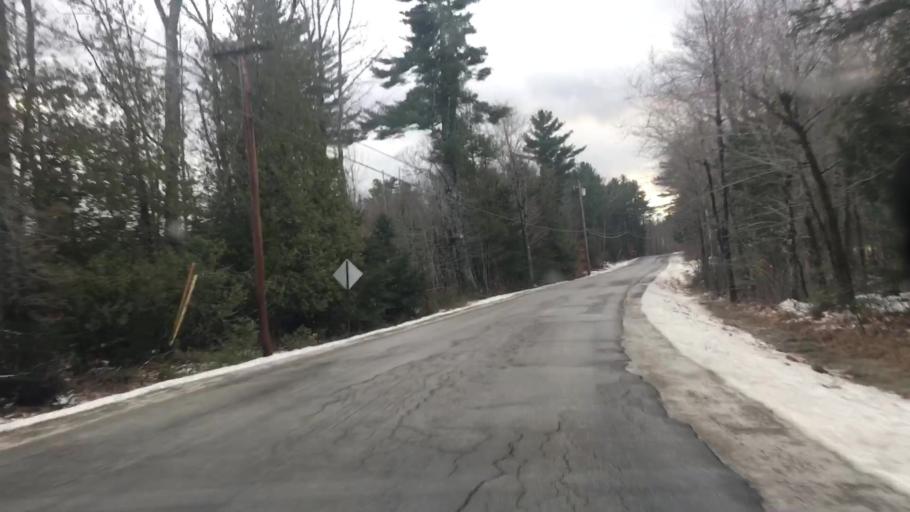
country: US
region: Maine
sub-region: Hancock County
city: Dedham
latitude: 44.6499
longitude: -68.7039
